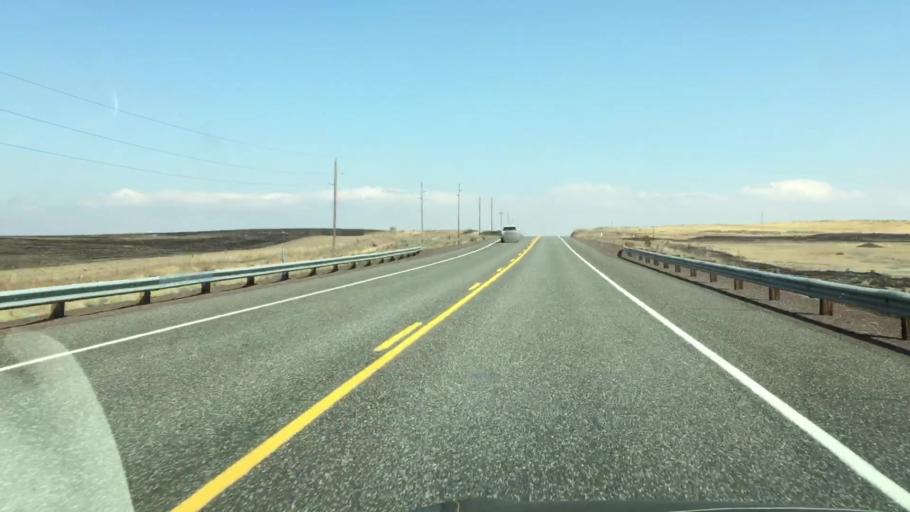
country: US
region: Oregon
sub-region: Wasco County
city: The Dalles
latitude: 45.3545
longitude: -121.1427
